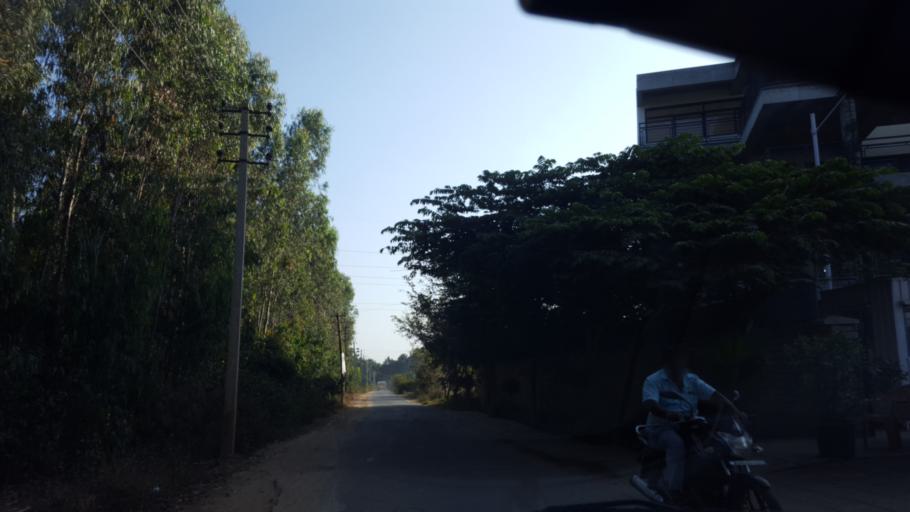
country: IN
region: Karnataka
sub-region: Bangalore Rural
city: Hoskote
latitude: 12.9210
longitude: 77.7570
